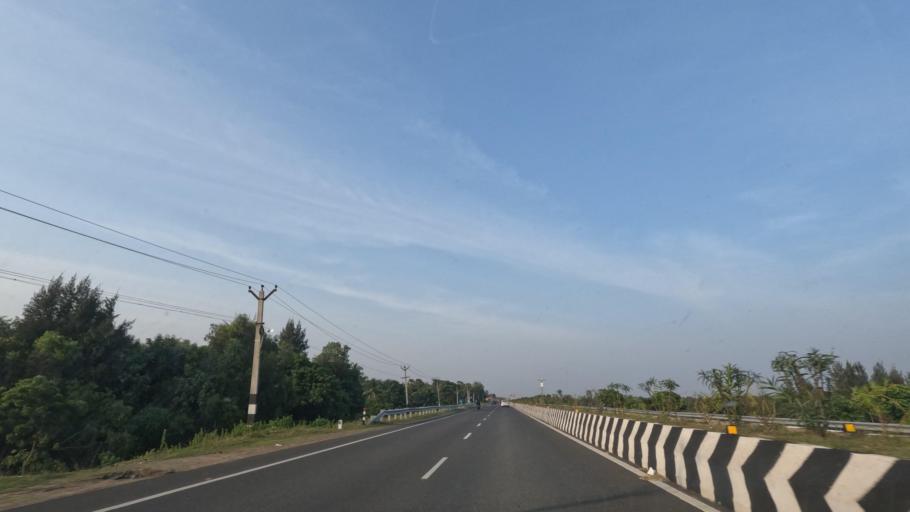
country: IN
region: Tamil Nadu
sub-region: Kancheepuram
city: Mamallapuram
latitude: 12.7125
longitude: 80.2258
